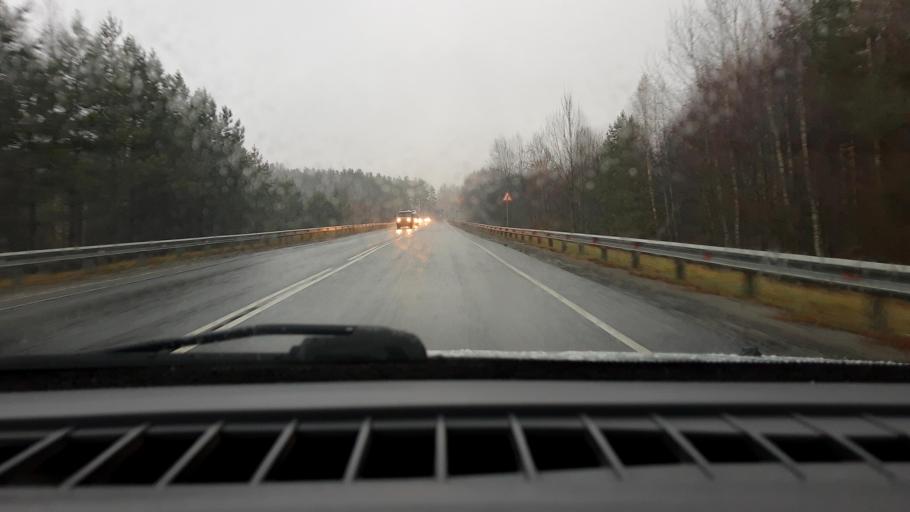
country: RU
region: Nizjnij Novgorod
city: Linda
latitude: 56.6625
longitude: 44.1300
